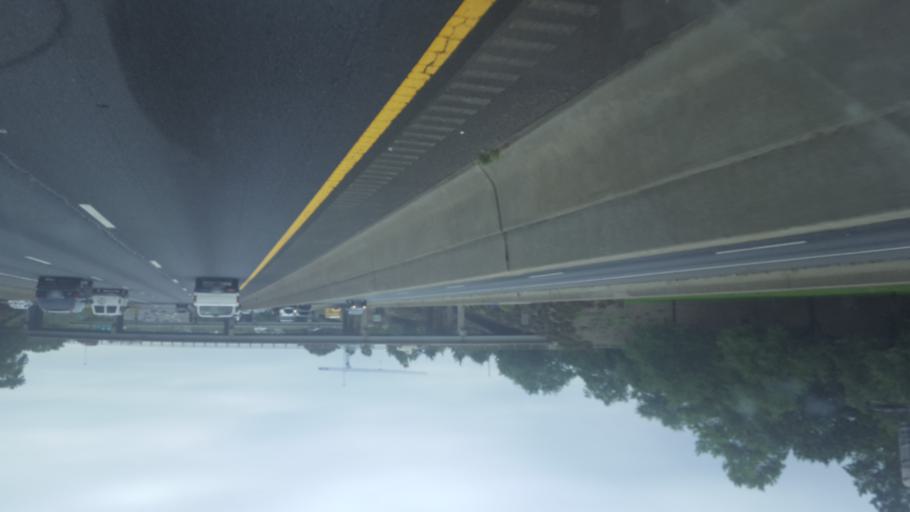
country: US
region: North Carolina
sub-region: Mecklenburg County
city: Charlotte
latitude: 35.2235
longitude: -80.8666
